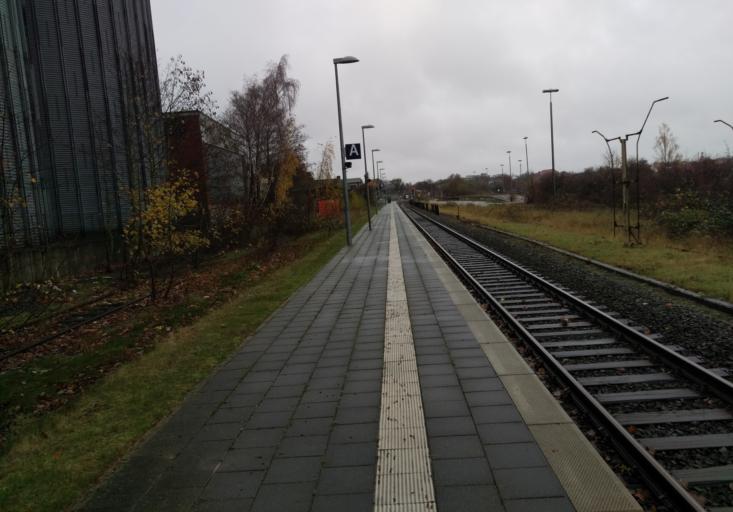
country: DE
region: Schleswig-Holstein
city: Oldenburg in Holstein
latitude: 54.2823
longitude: 10.8837
